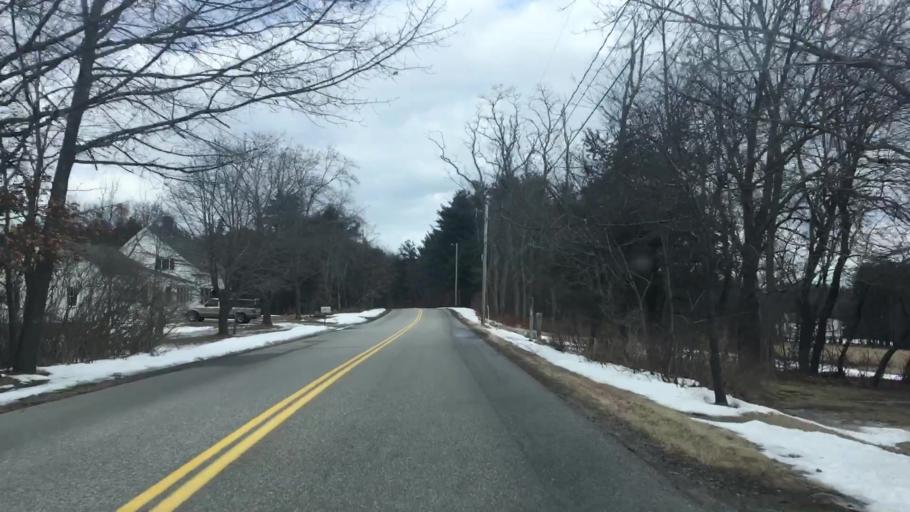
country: US
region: Maine
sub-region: York County
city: Wells Beach Station
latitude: 43.3104
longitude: -70.6538
